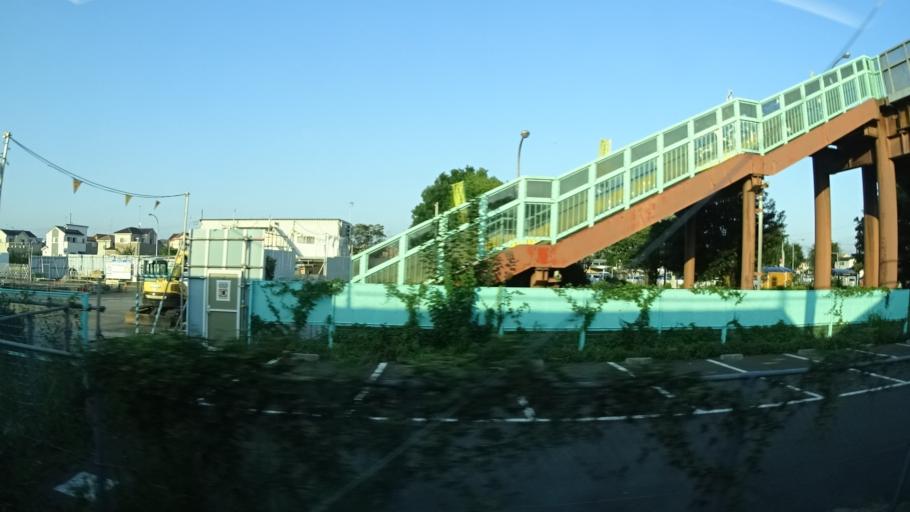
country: JP
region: Ibaraki
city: Ishioka
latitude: 36.2473
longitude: 140.2871
